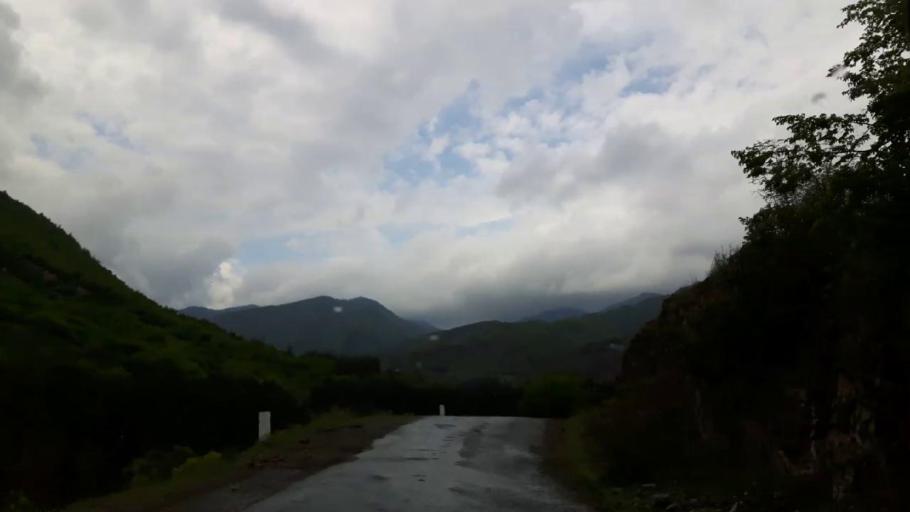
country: GE
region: Shida Kartli
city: Gori
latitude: 41.8954
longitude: 44.0367
